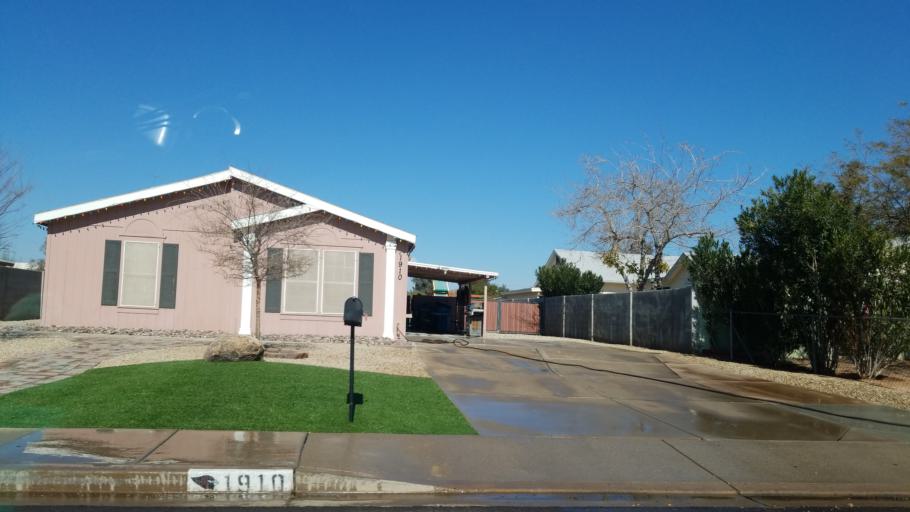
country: US
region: Arizona
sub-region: Maricopa County
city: Paradise Valley
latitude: 33.6478
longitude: -112.0418
